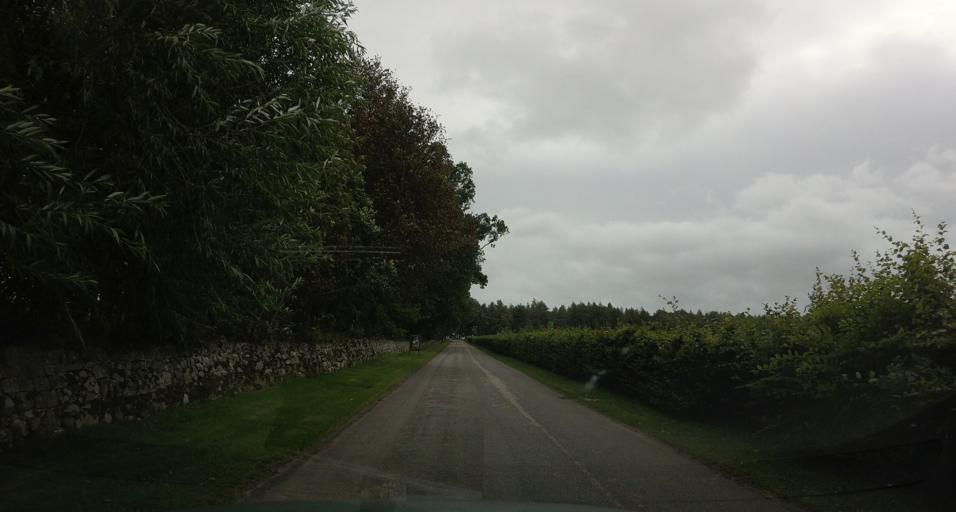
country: GB
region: Scotland
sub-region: Aberdeenshire
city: Kemnay
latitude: 57.2078
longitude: -2.4678
